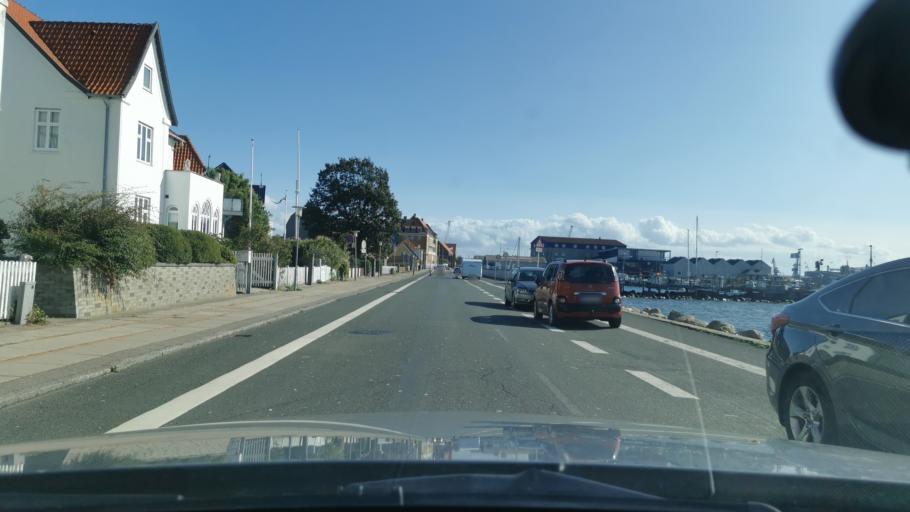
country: DK
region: Zealand
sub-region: Kalundborg Kommune
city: Kalundborg
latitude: 55.6786
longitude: 11.0807
